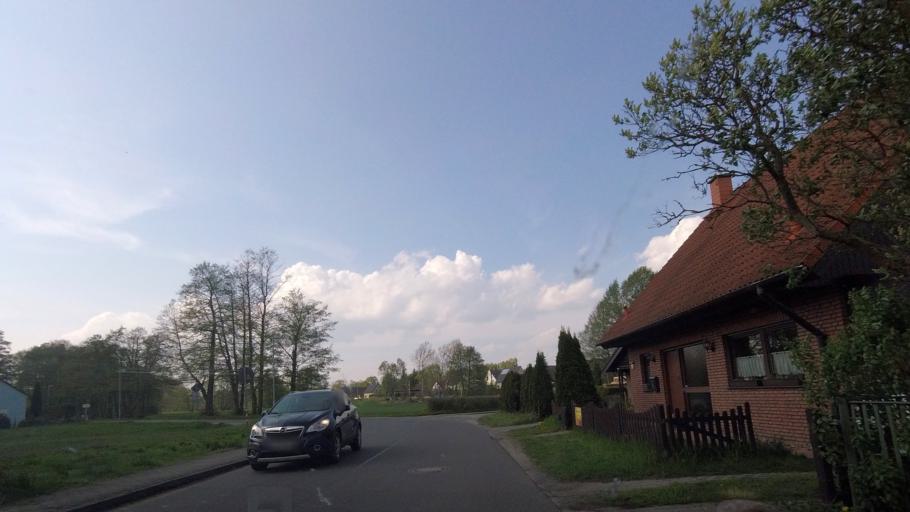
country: DE
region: Saxony-Anhalt
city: Zahna
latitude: 51.9203
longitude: 12.7891
